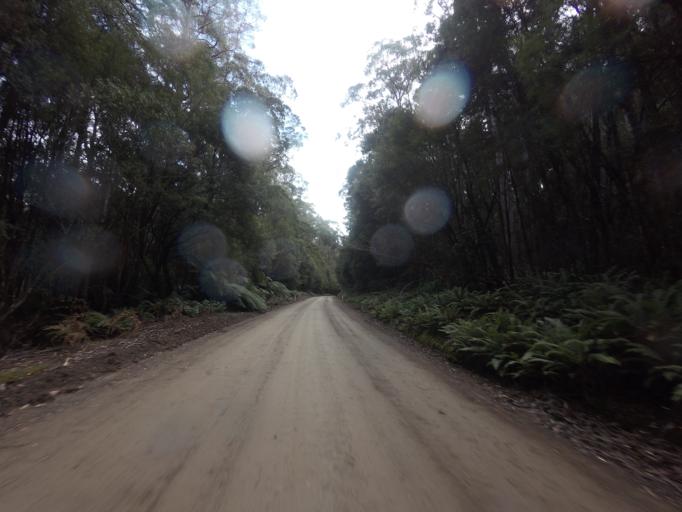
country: AU
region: Tasmania
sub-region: Huon Valley
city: Geeveston
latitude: -43.3924
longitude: 146.8543
